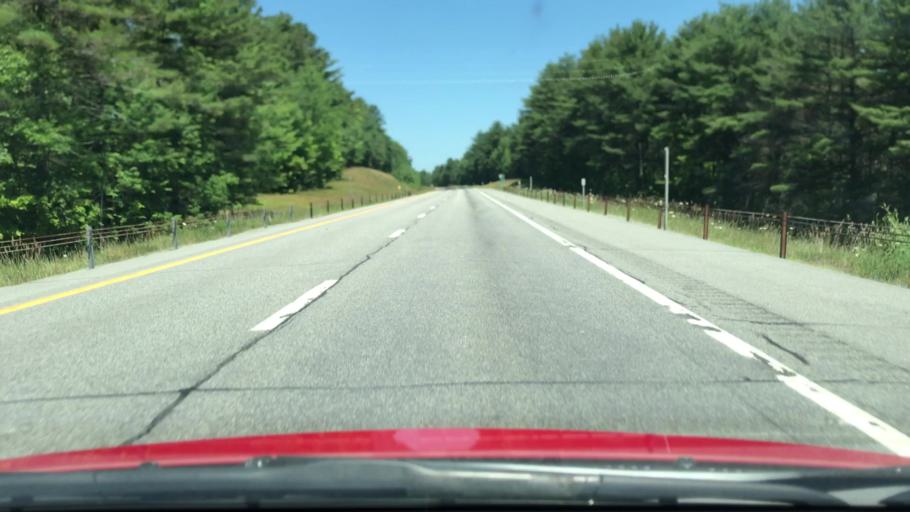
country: US
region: New York
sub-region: Essex County
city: Elizabethtown
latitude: 44.1488
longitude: -73.5830
